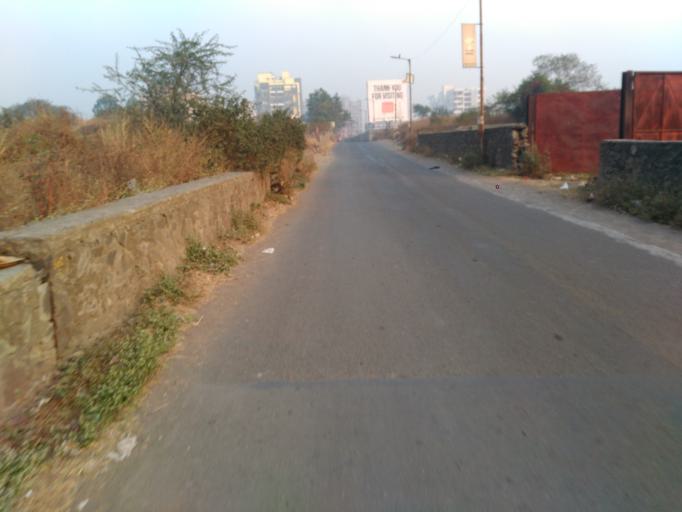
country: IN
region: Maharashtra
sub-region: Pune Division
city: Pune
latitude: 18.4505
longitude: 73.8841
